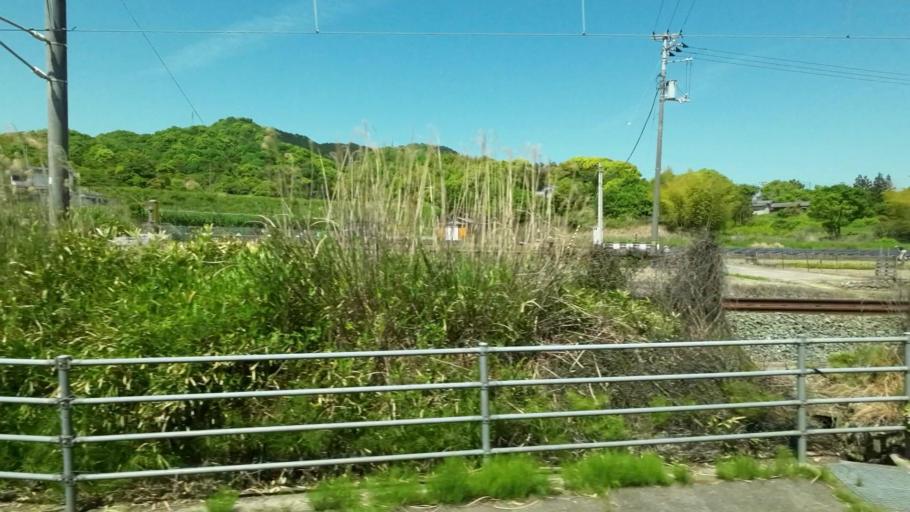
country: JP
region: Ehime
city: Hojo
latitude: 34.0848
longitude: 132.9845
